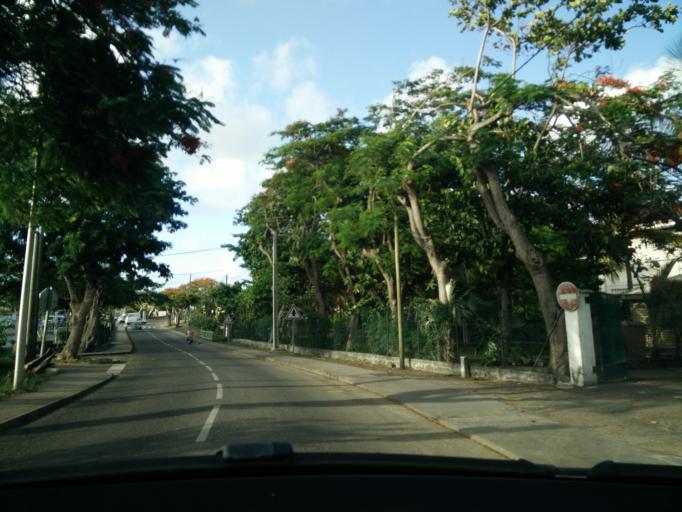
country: GP
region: Guadeloupe
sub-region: Guadeloupe
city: Le Moule
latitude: 16.3251
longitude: -61.3442
